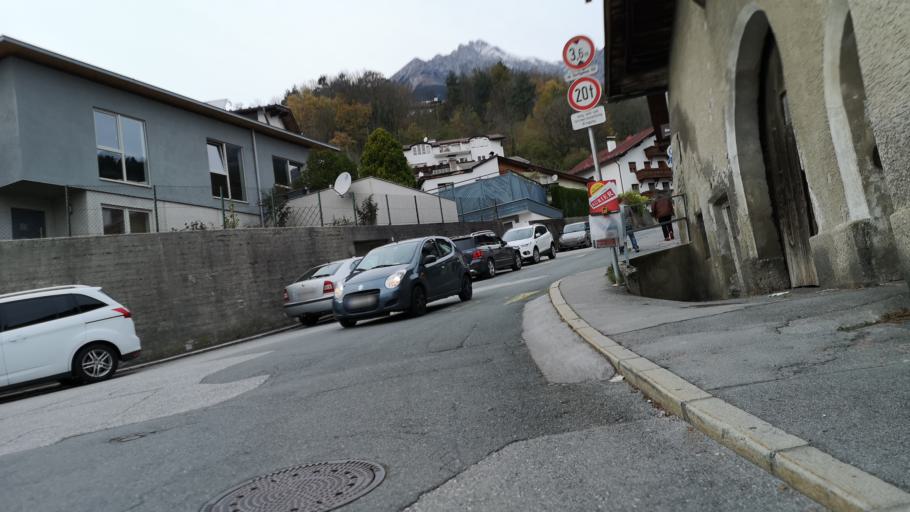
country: AT
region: Tyrol
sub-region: Innsbruck Stadt
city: Innsbruck
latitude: 47.2719
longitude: 11.3818
